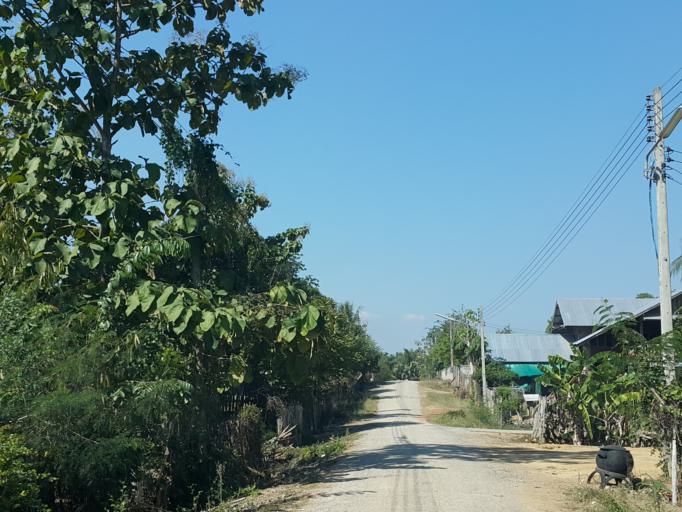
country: TH
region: Sukhothai
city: Thung Saliam
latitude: 17.3437
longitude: 99.4439
